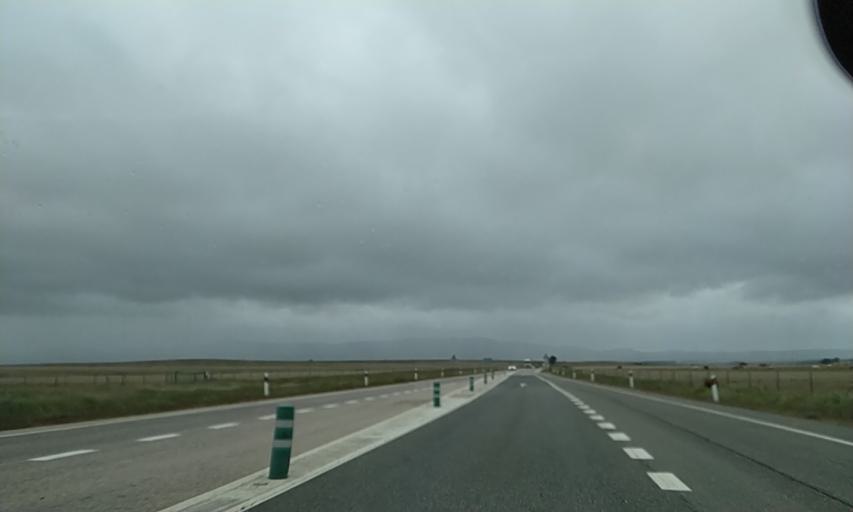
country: ES
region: Extremadura
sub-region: Provincia de Caceres
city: Malpartida de Caceres
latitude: 39.3615
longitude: -6.4631
